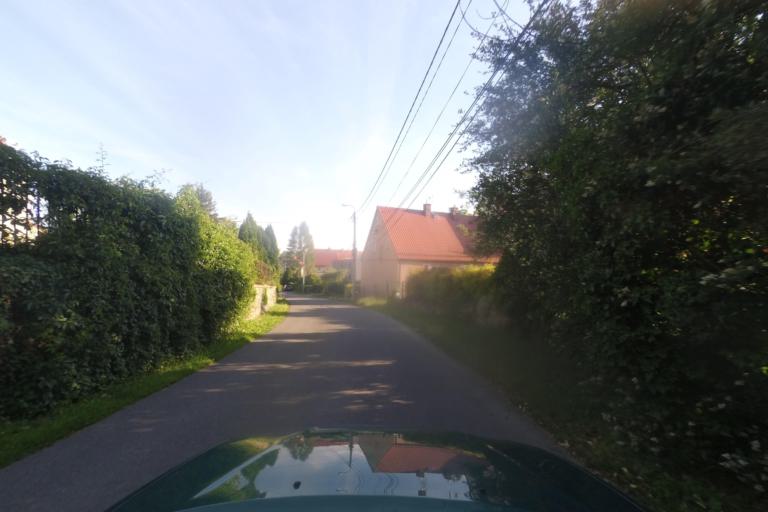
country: PL
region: Lower Silesian Voivodeship
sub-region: Powiat dzierzoniowski
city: Niemcza
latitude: 50.7199
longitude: 16.8319
